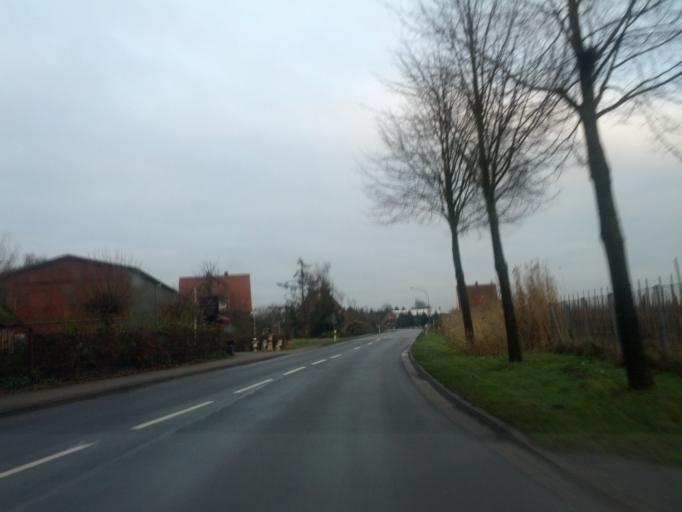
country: DE
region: Lower Saxony
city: Mittelnkirchen
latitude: 53.5397
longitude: 9.6242
